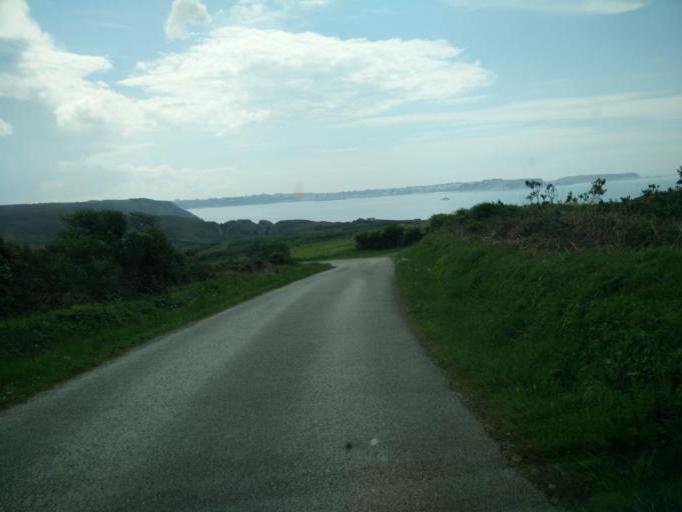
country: FR
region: Brittany
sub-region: Departement du Finistere
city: Roscanvel
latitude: 48.3112
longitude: -4.5703
